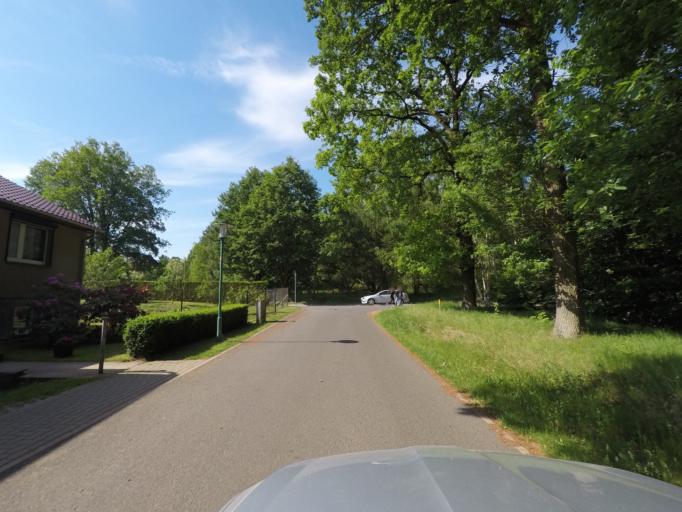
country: DE
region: Brandenburg
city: Melchow
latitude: 52.8648
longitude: 13.7151
